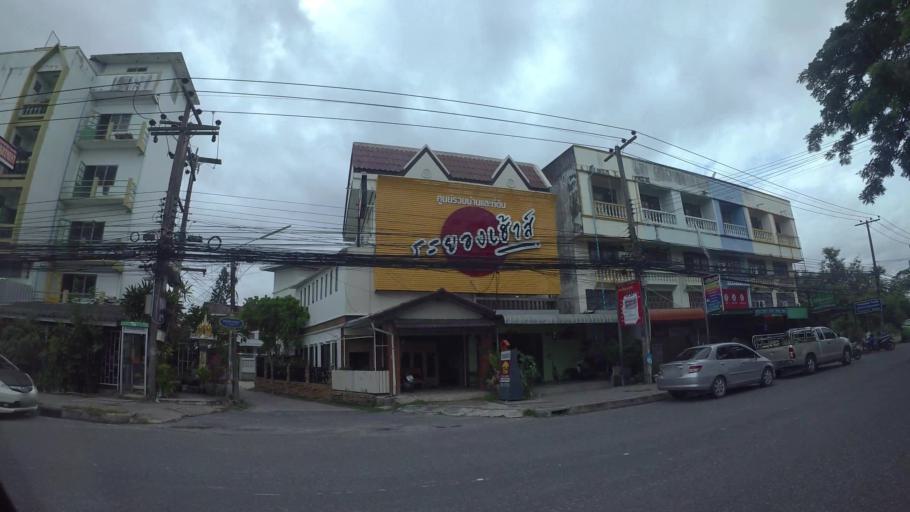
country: TH
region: Rayong
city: Rayong
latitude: 12.6701
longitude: 101.2750
